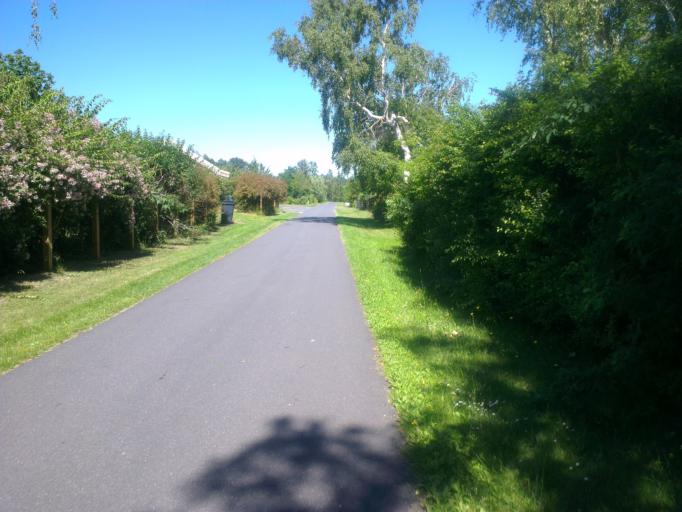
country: DK
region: Capital Region
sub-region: Halsnaes Kommune
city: Hundested
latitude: 55.9179
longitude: 11.9066
